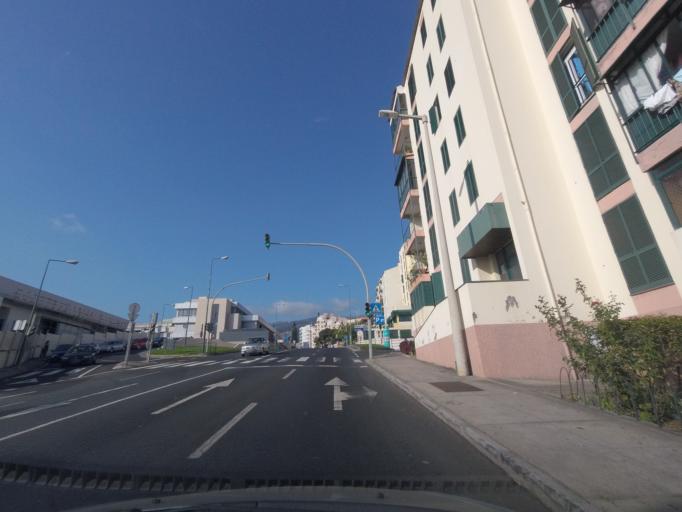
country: PT
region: Madeira
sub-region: Funchal
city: Funchal
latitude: 32.6463
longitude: -16.9226
